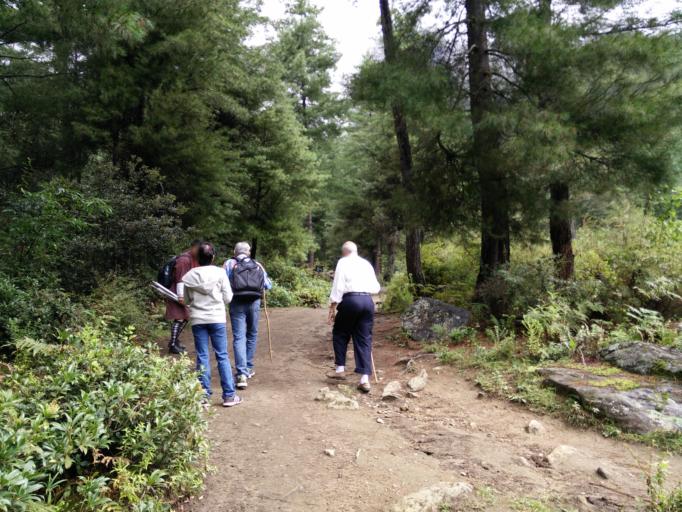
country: BT
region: Paro
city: Paro
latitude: 27.4835
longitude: 89.3611
